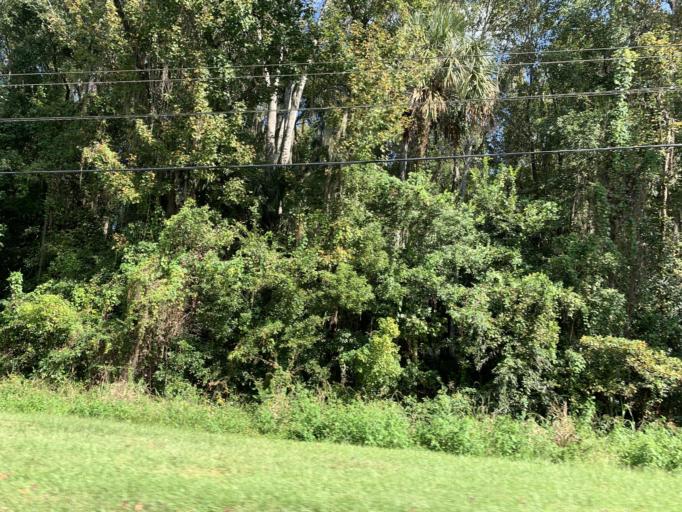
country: US
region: Florida
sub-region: Marion County
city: Ocala
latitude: 29.1739
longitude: -82.1304
